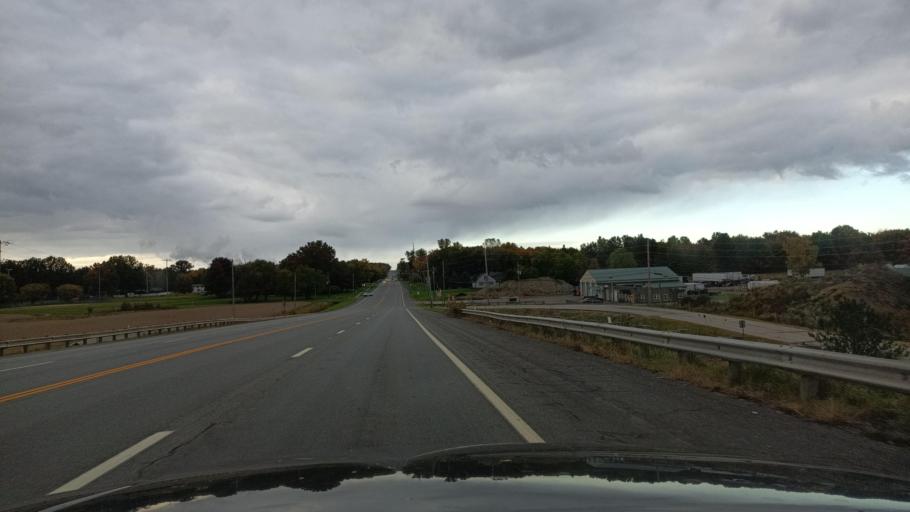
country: US
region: Ohio
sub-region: Trumbull County
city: Lordstown
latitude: 41.1771
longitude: -80.8575
